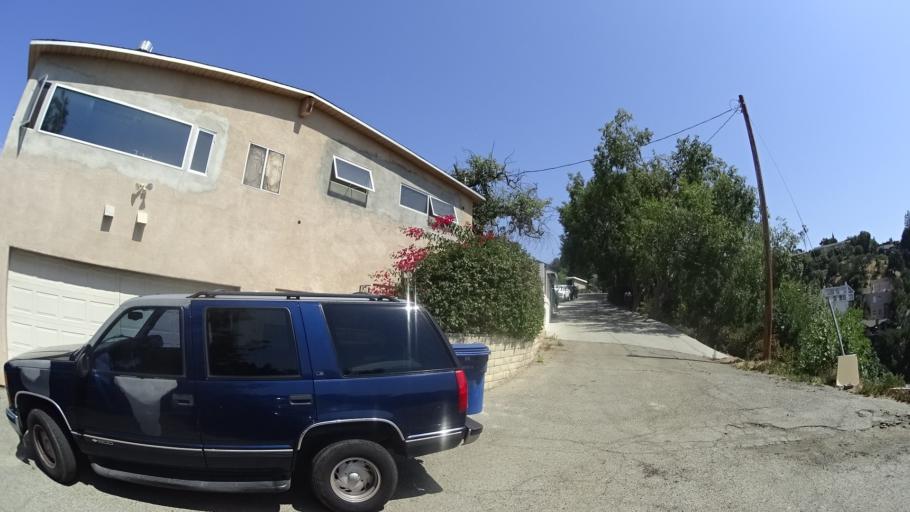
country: US
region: California
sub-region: Los Angeles County
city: North Hollywood
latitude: 34.1412
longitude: -118.4048
